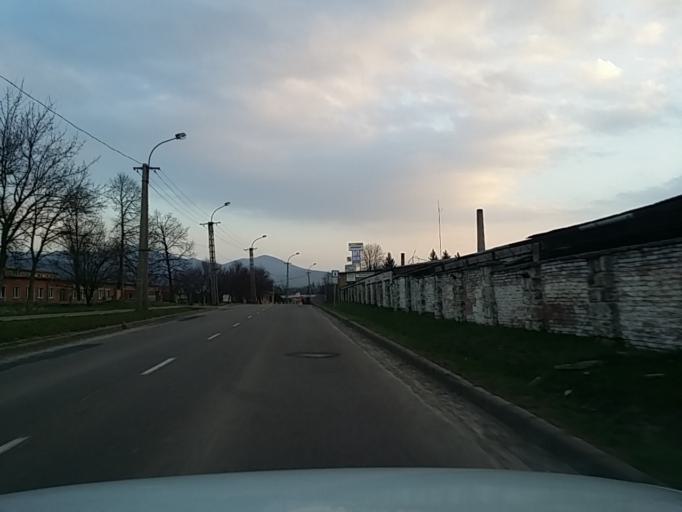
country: HU
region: Nograd
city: Batonyterenye
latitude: 47.9826
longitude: 19.8232
